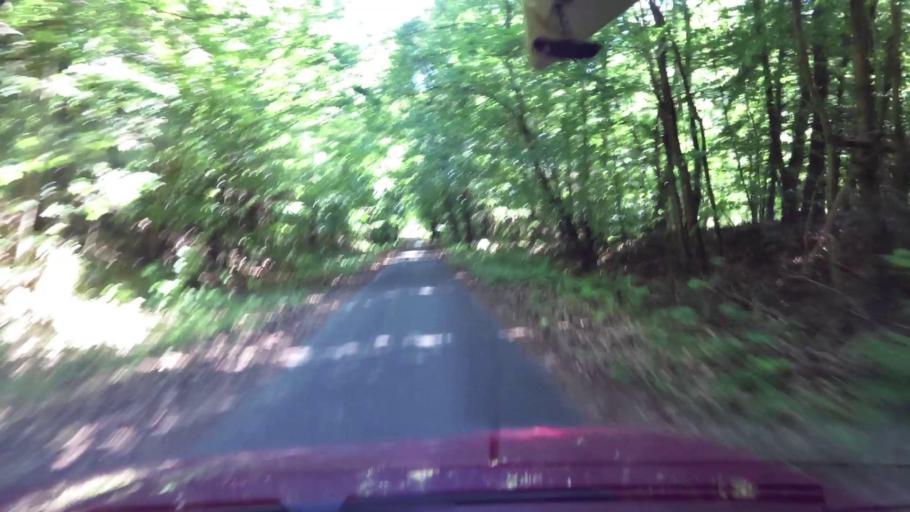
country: PL
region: West Pomeranian Voivodeship
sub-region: Powiat koszalinski
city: Polanow
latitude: 54.0346
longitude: 16.7928
